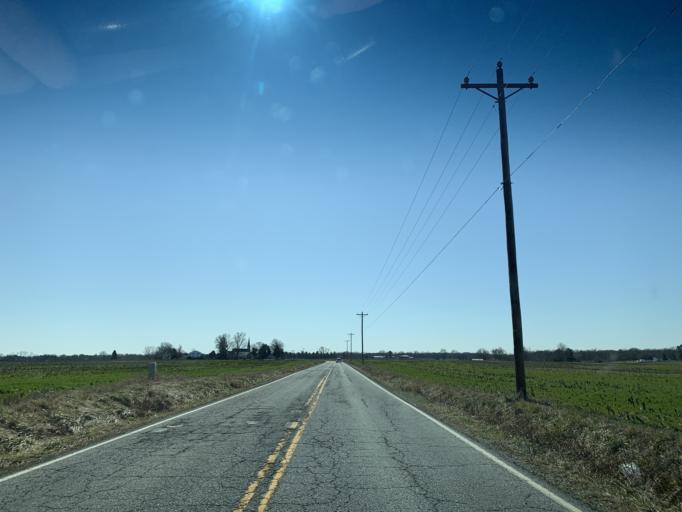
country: US
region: Maryland
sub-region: Cecil County
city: Charlestown
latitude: 39.4307
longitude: -75.9151
